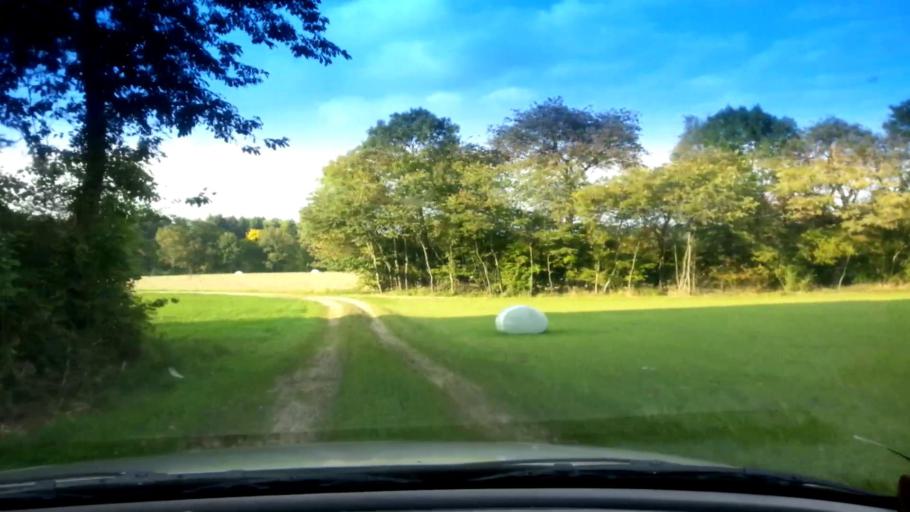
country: DE
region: Bavaria
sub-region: Upper Franconia
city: Wattendorf
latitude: 49.9950
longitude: 11.0995
